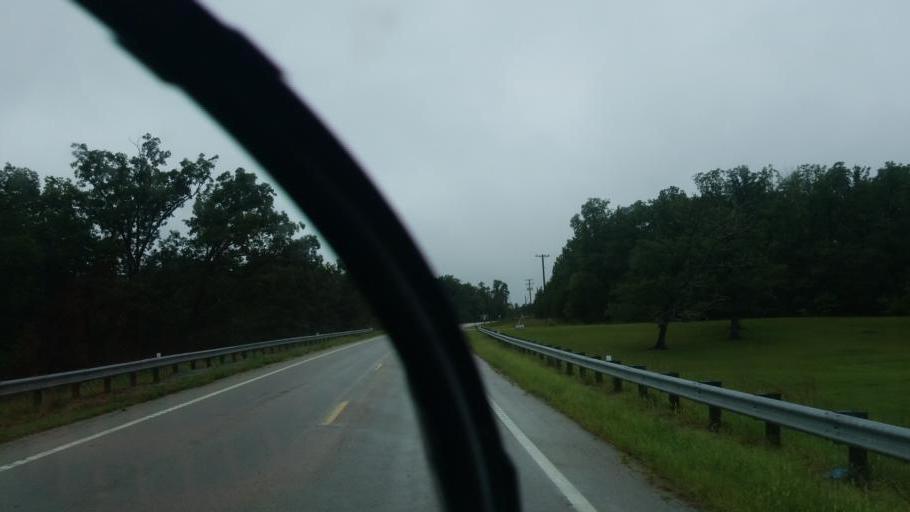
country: US
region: Ohio
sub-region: Adams County
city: West Union
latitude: 38.7952
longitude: -83.5178
